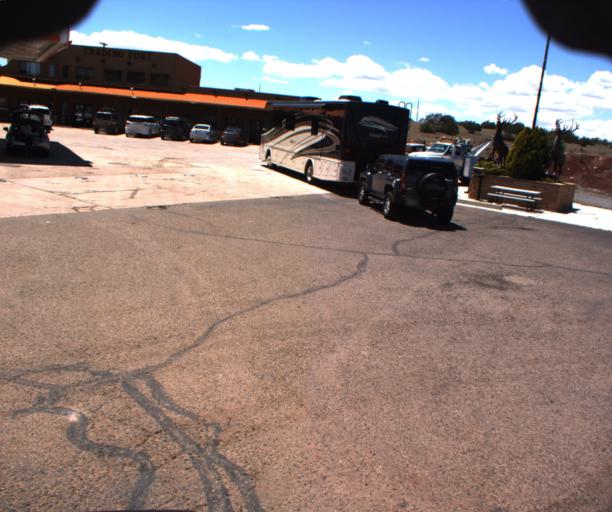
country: US
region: Arizona
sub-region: Coconino County
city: Williams
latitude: 35.2188
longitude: -112.4983
